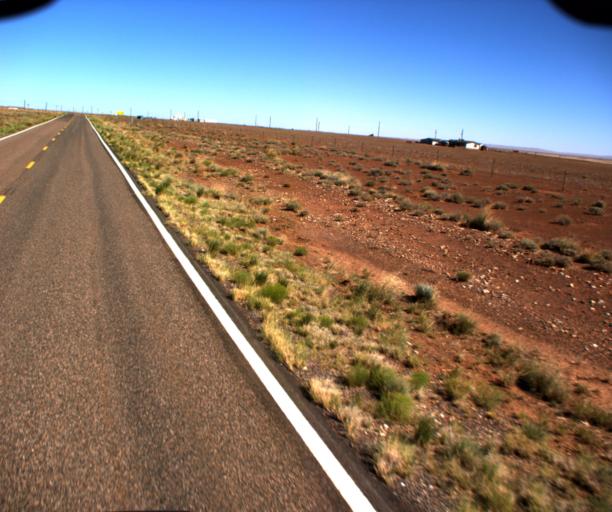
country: US
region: Arizona
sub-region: Coconino County
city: LeChee
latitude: 35.1349
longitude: -110.8853
